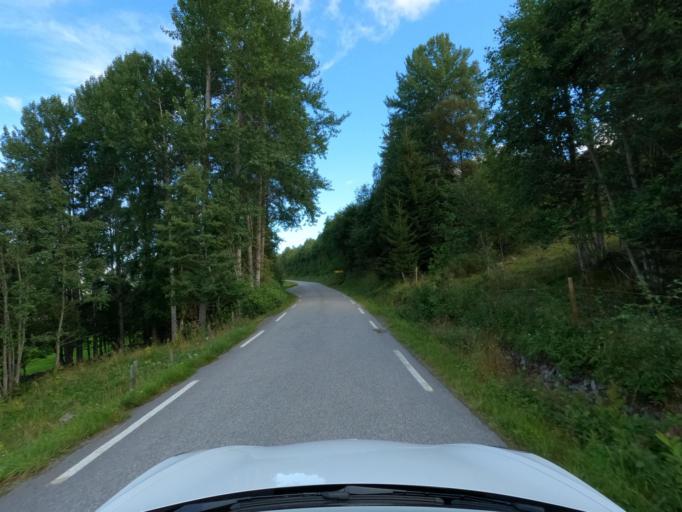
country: NO
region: Buskerud
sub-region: Nore og Uvdal
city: Rodberg
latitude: 60.0376
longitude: 8.8325
